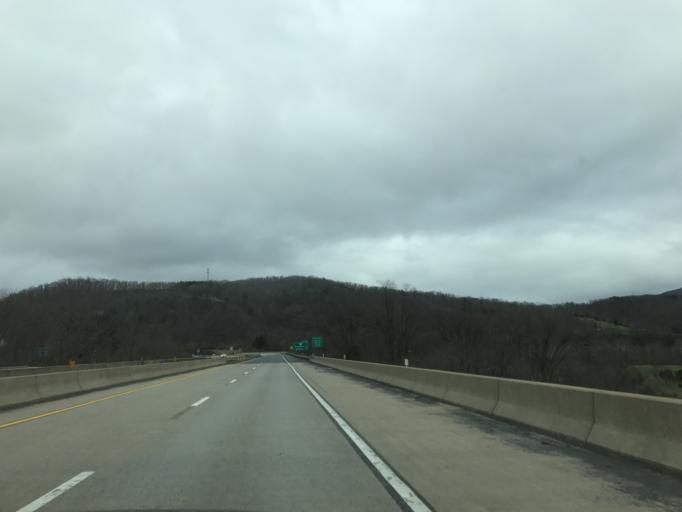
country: US
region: West Virginia
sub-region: Summers County
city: Hinton
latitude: 37.7809
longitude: -80.8996
